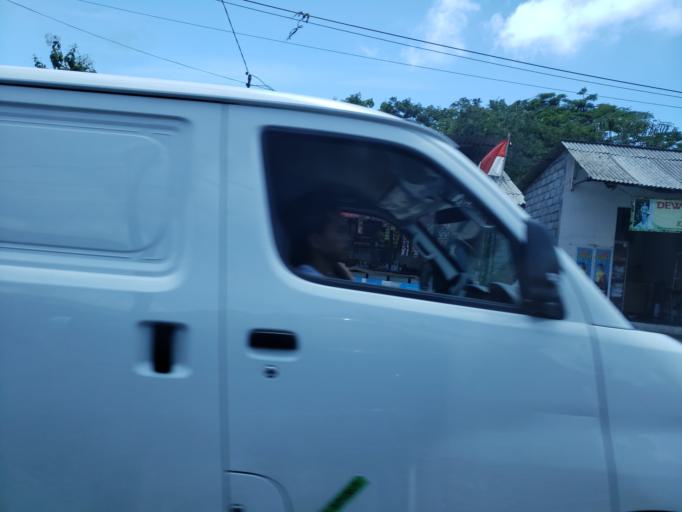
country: ID
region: Bali
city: Kangin
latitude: -8.8308
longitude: 115.1323
